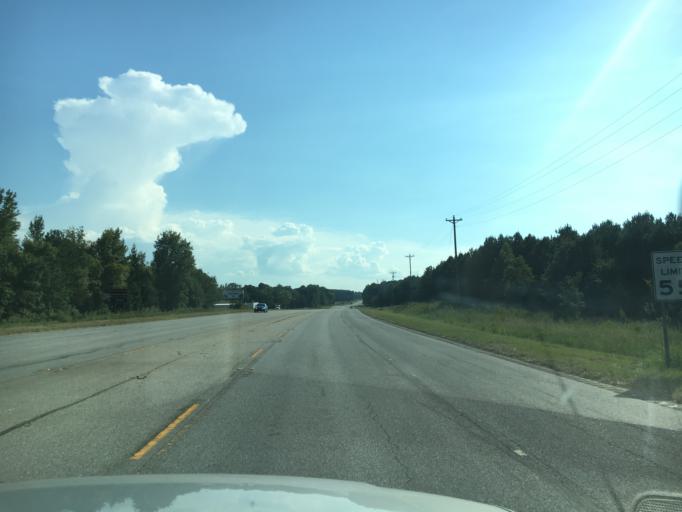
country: US
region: South Carolina
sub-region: Laurens County
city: Clinton
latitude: 34.4339
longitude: -81.8968
